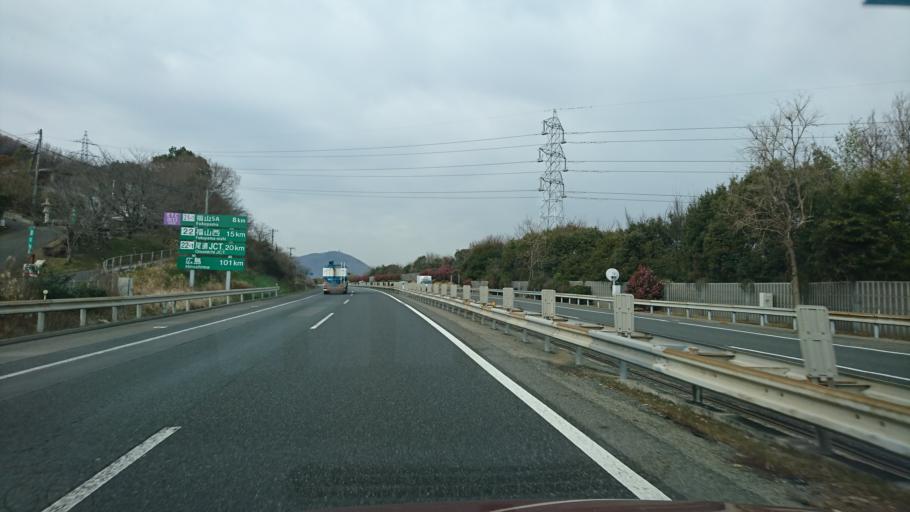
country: JP
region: Hiroshima
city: Fukuyama
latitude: 34.5165
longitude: 133.3865
